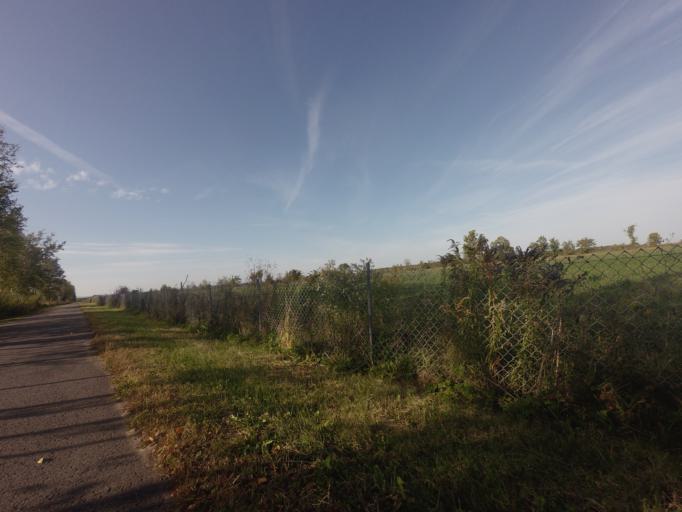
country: CA
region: Quebec
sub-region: Laurentides
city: Blainville
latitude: 45.7156
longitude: -73.9233
